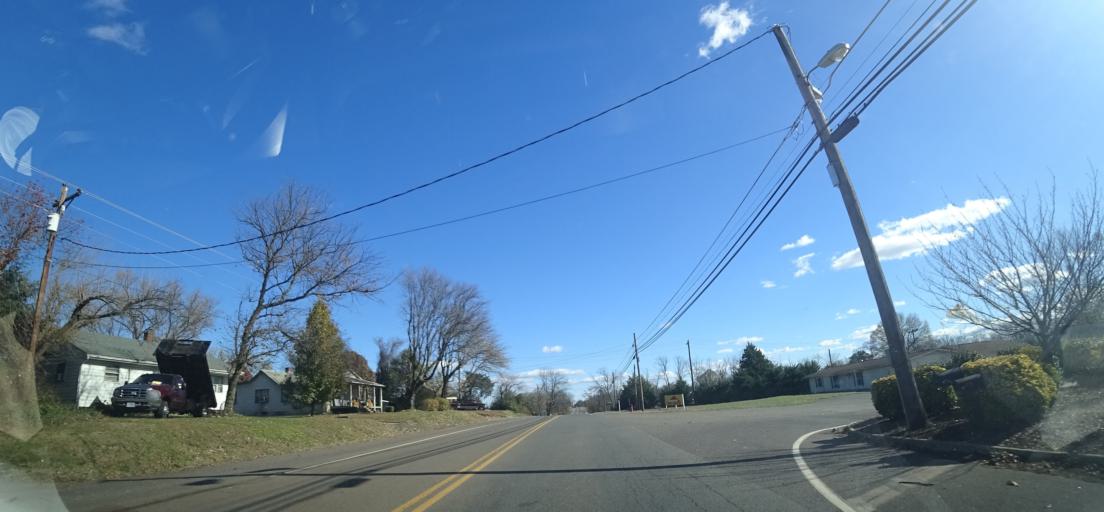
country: US
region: Virginia
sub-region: Culpeper County
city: Culpeper
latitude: 38.4866
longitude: -77.9521
